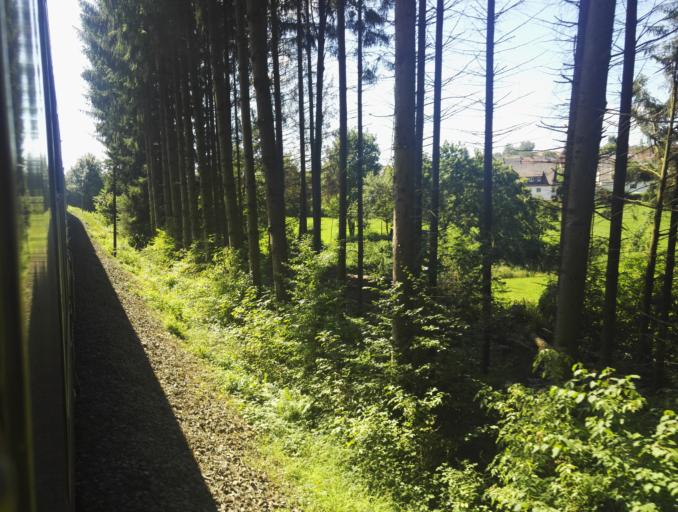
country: DE
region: Baden-Wuerttemberg
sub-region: Regierungsbezirk Stuttgart
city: Welzheim
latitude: 48.8616
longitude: 9.6271
